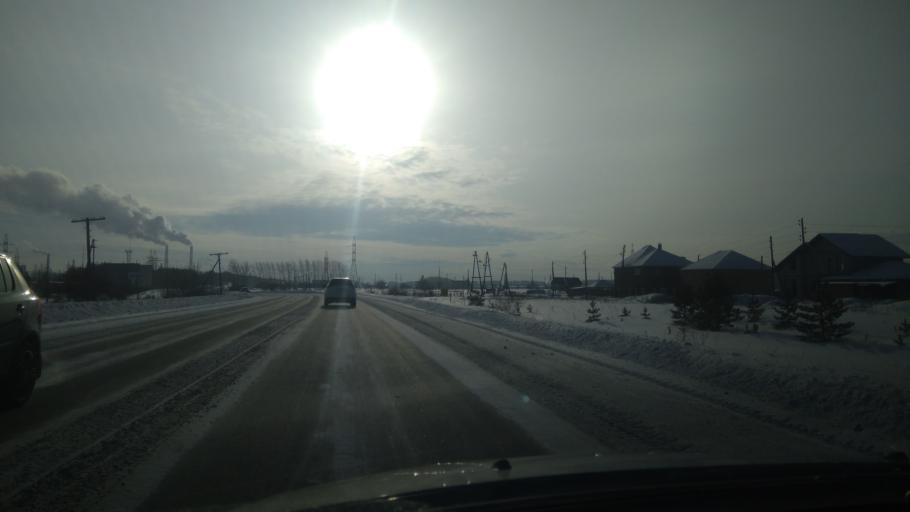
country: RU
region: Sverdlovsk
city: Sukhoy Log
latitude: 56.8853
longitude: 62.0422
